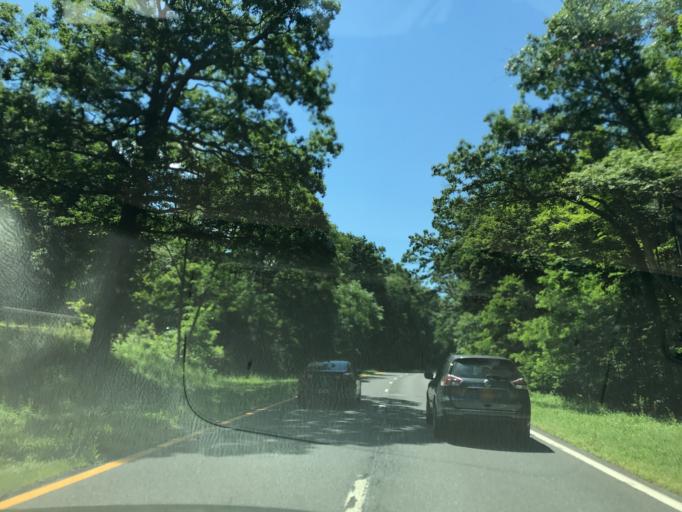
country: US
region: New York
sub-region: Dutchess County
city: Pleasant Valley
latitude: 41.6997
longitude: -73.7836
